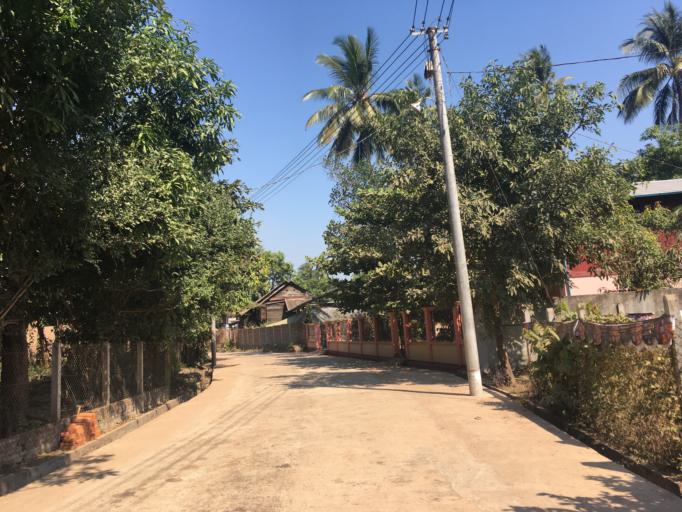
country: MM
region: Mon
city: Mawlamyine
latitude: 16.4326
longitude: 97.7055
